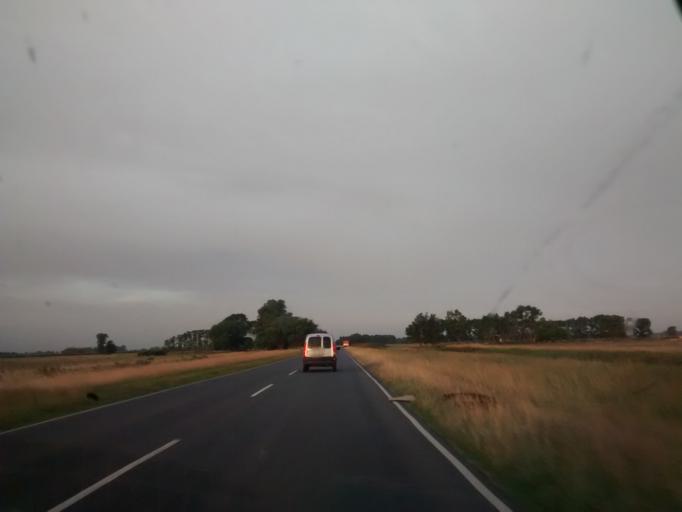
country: AR
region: Buenos Aires
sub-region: Partido de General Belgrano
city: General Belgrano
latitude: -35.8092
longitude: -58.5627
